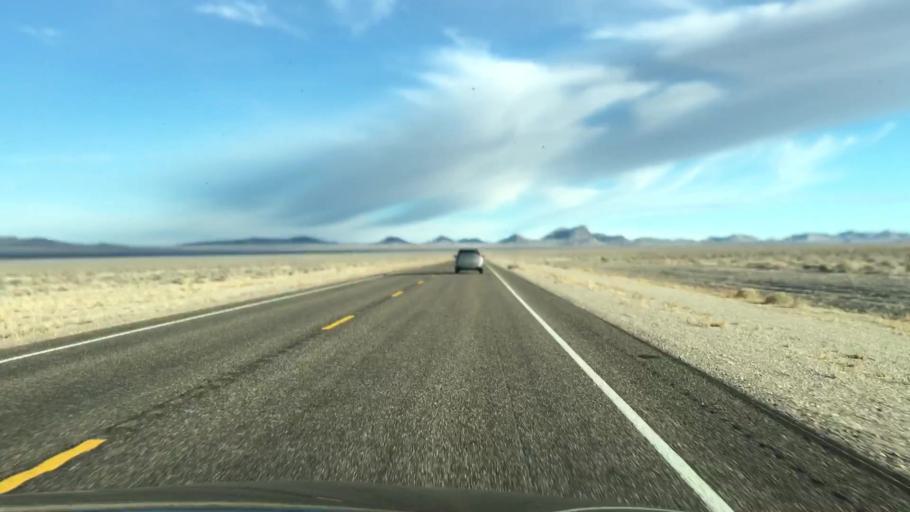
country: US
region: Nevada
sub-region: Nye County
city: Tonopah
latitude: 38.1249
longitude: -117.4065
